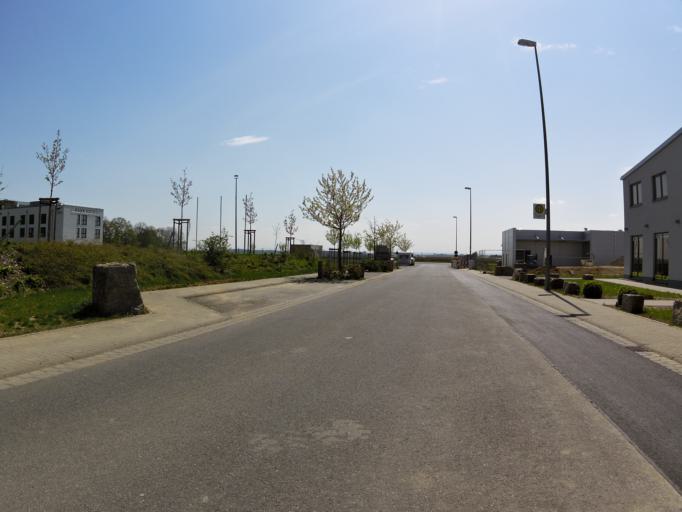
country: DE
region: Bavaria
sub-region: Regierungsbezirk Unterfranken
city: Giebelstadt
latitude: 49.6889
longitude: 9.9449
